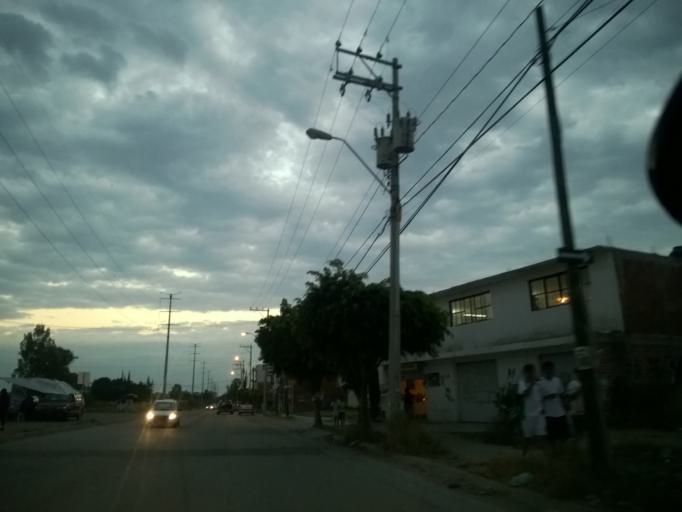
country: MX
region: Guanajuato
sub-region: Leon
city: Fraccionamiento Paraiso Real
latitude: 21.0723
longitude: -101.6122
